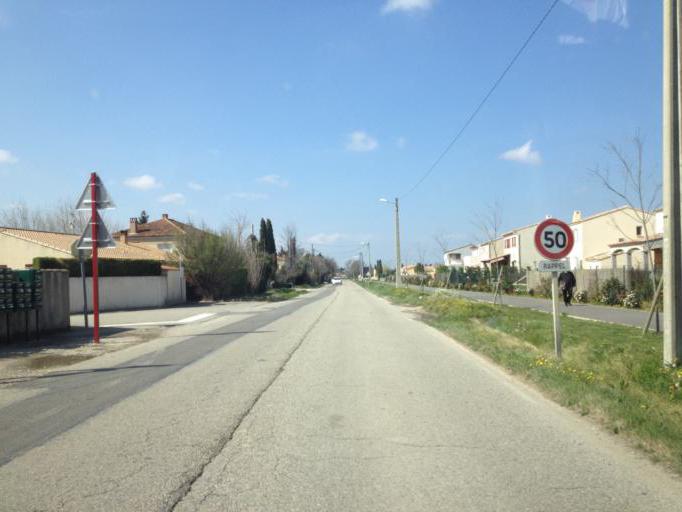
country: FR
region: Provence-Alpes-Cote d'Azur
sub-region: Departement du Vaucluse
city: Jonquieres
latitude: 44.1207
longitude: 4.9109
